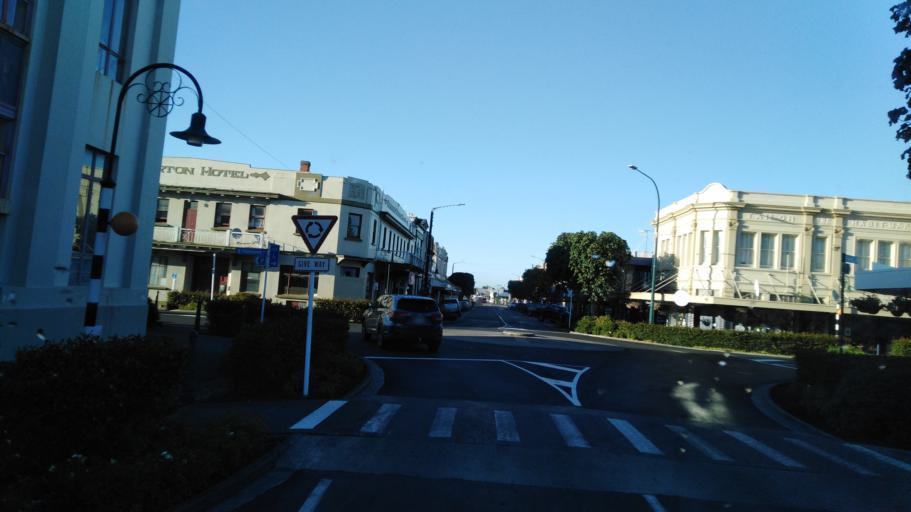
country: NZ
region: Manawatu-Wanganui
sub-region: Rangitikei District
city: Bulls
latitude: -40.0671
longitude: 175.3789
